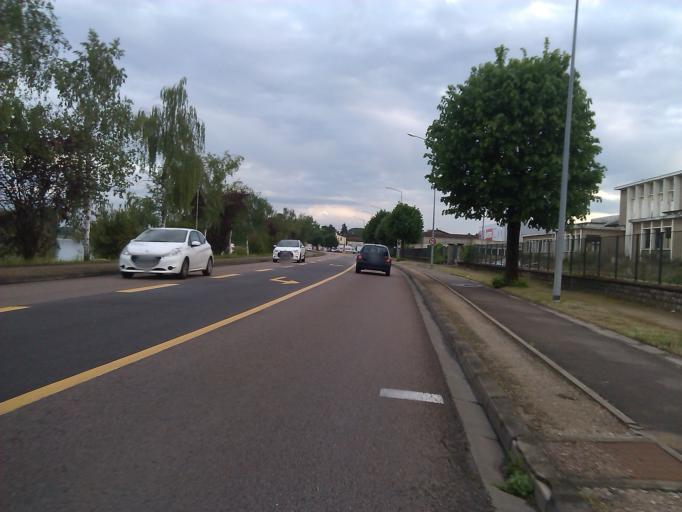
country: FR
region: Bourgogne
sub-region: Departement de Saone-et-Loire
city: Saint-Remy
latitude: 46.7711
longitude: 4.8437
